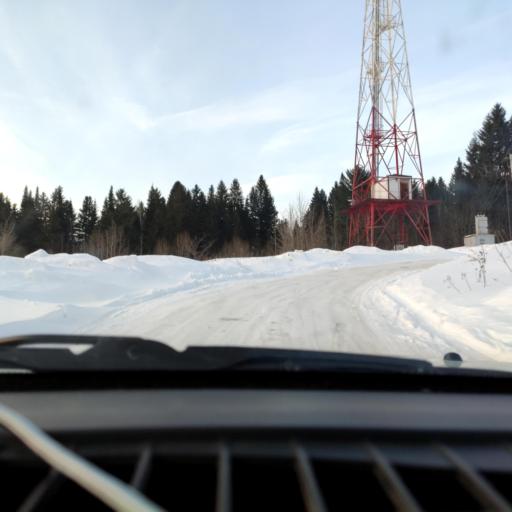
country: RU
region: Perm
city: Ferma
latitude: 57.9646
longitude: 56.3779
